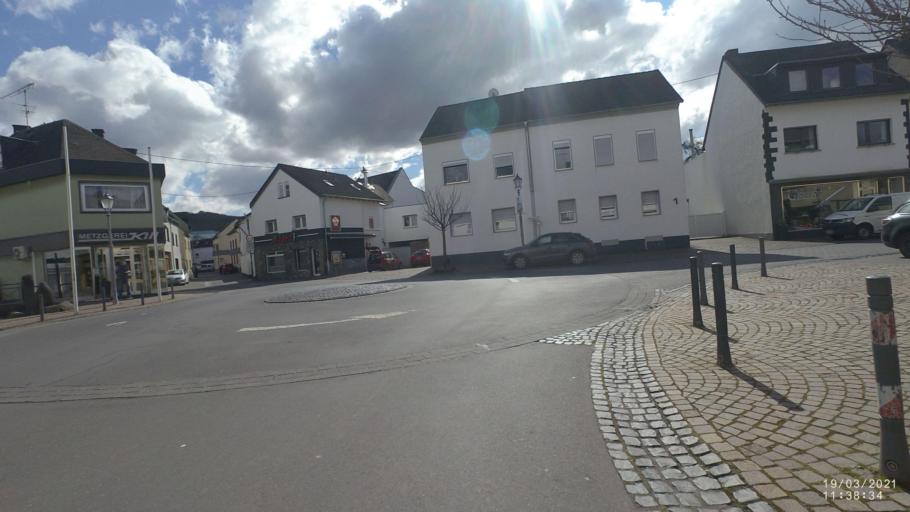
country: DE
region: Rheinland-Pfalz
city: Kruft
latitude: 50.3860
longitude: 7.3406
